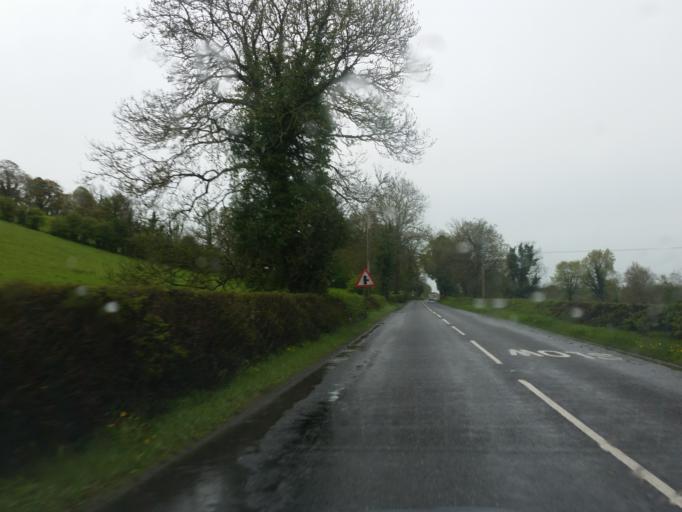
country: GB
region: Northern Ireland
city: Lisnaskea
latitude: 54.2253
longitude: -7.4143
